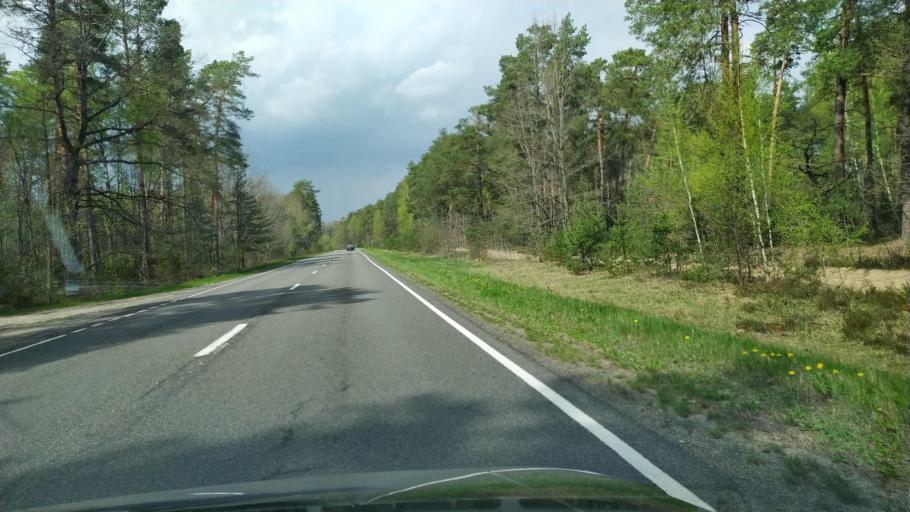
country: BY
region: Brest
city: Pruzhany
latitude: 52.4090
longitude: 24.5590
